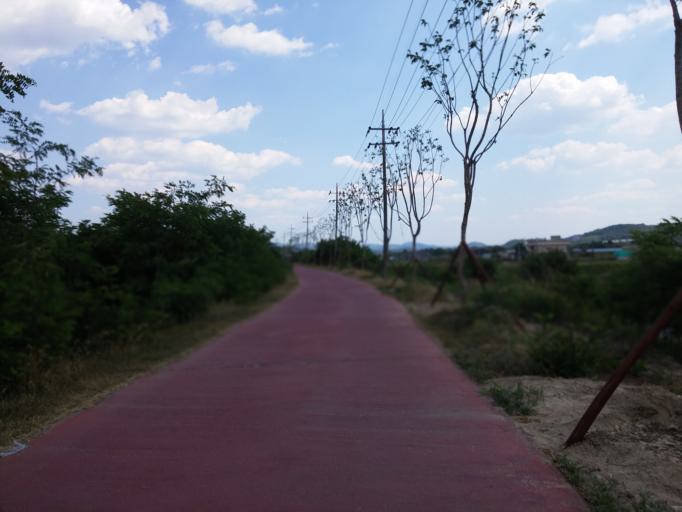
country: KR
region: Chungcheongbuk-do
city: Cheongju-si
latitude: 36.5909
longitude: 127.4974
